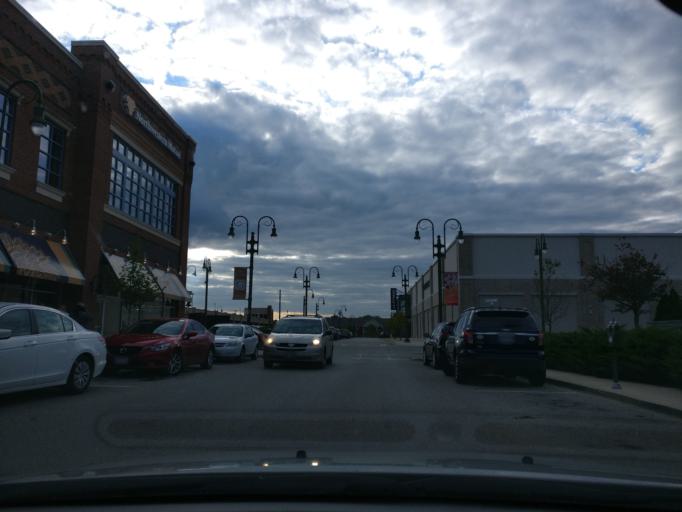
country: US
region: Ohio
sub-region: Greene County
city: Beavercreek
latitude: 39.6949
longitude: -84.1037
